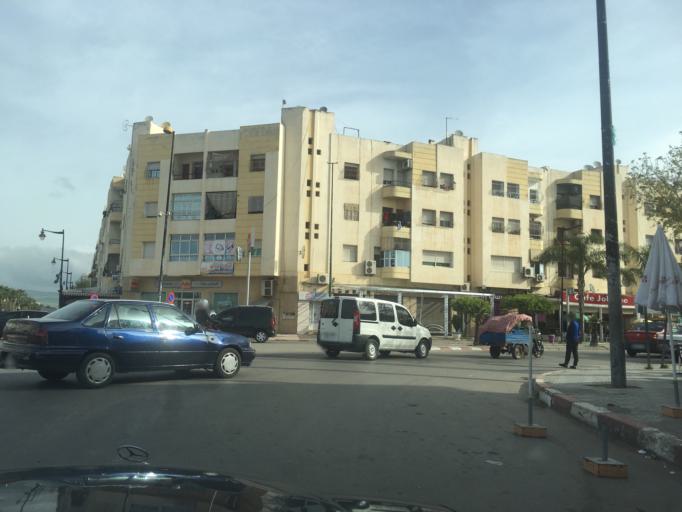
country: MA
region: Fes-Boulemane
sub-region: Fes
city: Fes
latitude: 34.0177
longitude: -5.0524
